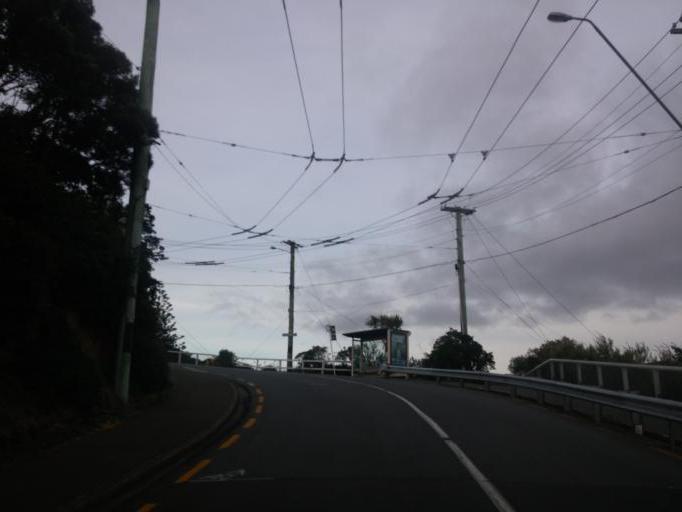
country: NZ
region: Wellington
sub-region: Wellington City
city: Brooklyn
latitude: -41.3093
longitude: 174.7658
